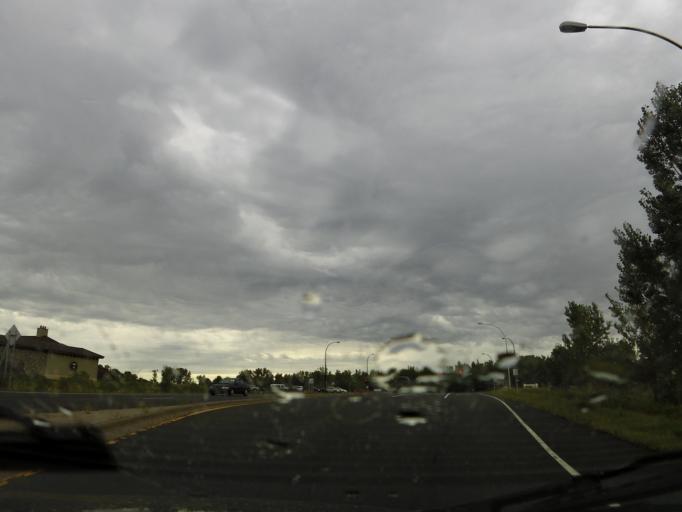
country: US
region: Minnesota
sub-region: Washington County
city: Woodbury
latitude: 44.9379
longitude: -92.9580
